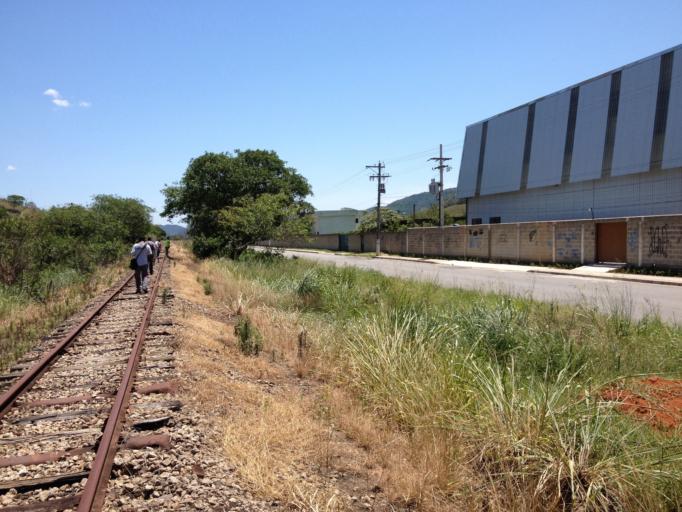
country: BR
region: Rio de Janeiro
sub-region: Rio Bonito
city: Rio Bonito
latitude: -22.7077
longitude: -42.6624
